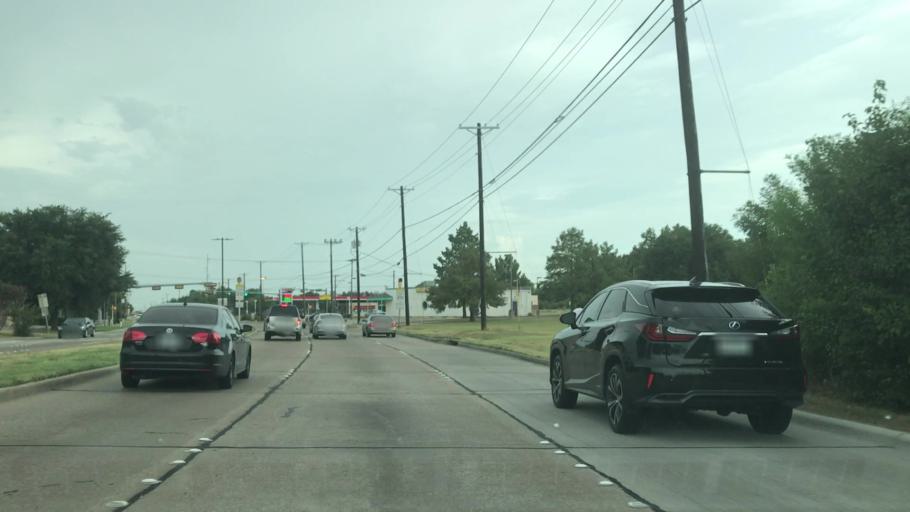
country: US
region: Texas
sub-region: Dallas County
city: Rowlett
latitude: 32.8590
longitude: -96.6030
